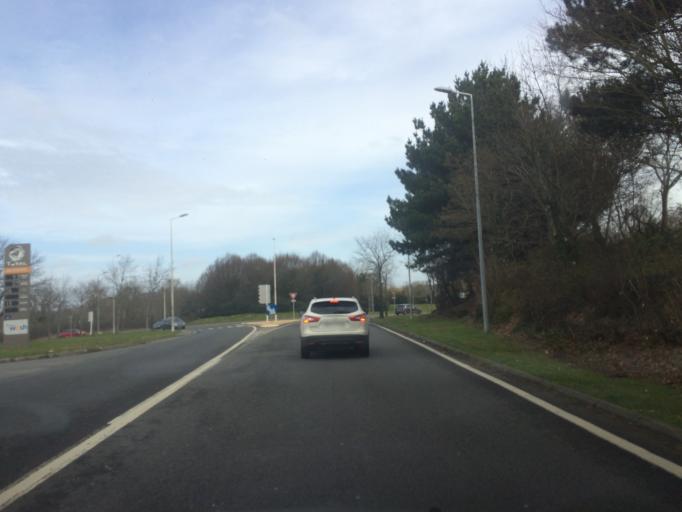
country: FR
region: Pays de la Loire
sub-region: Departement de la Loire-Atlantique
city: Saint-Nazaire
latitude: 47.2704
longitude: -2.2504
